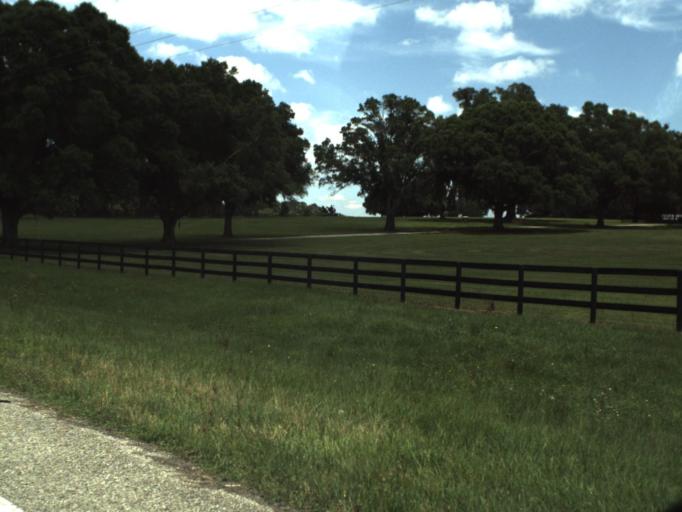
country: US
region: Florida
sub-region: Marion County
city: Citra
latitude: 29.3918
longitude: -82.1924
